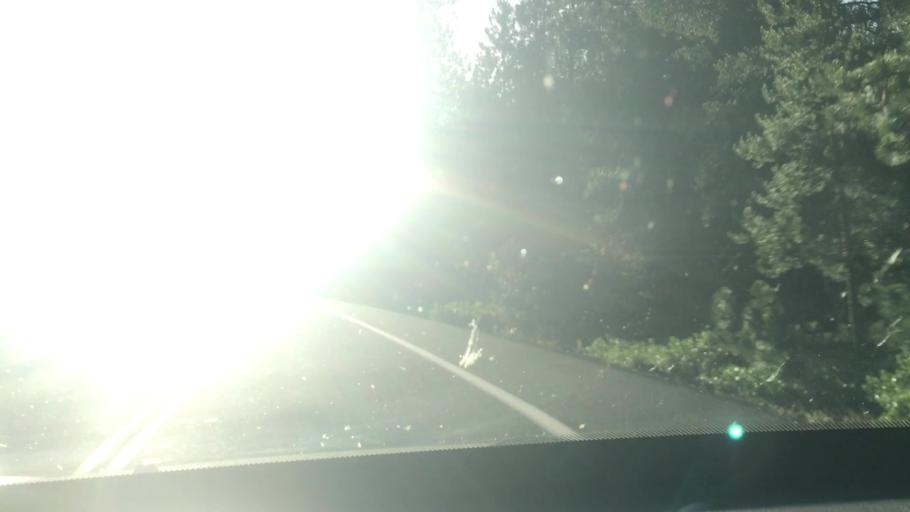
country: US
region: Oregon
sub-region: Deschutes County
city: Deschutes River Woods
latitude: 44.0396
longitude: -121.4648
